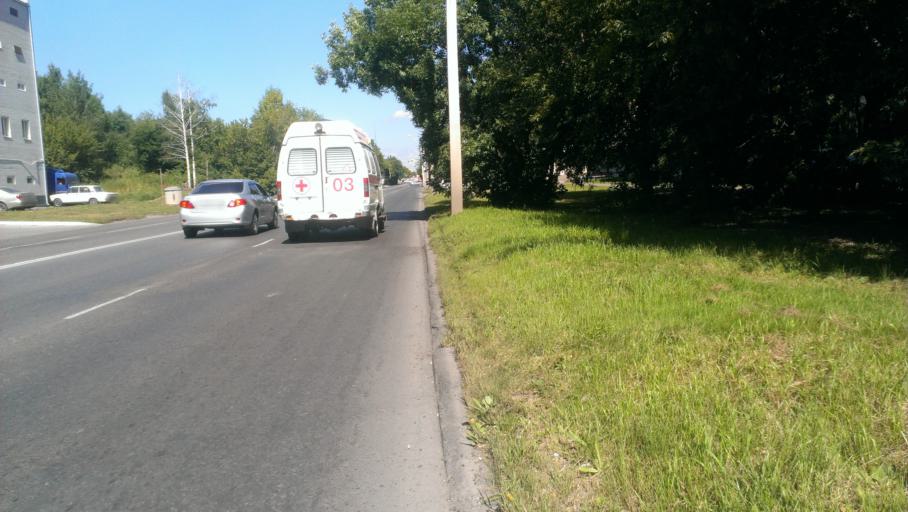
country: RU
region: Altai Krai
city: Novosilikatnyy
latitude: 53.3639
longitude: 83.6605
